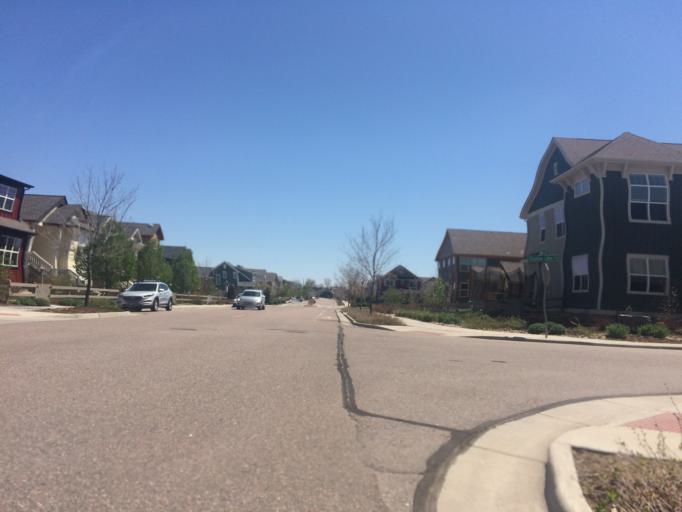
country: US
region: Colorado
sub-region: Boulder County
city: Louisville
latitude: 39.9975
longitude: -105.1332
